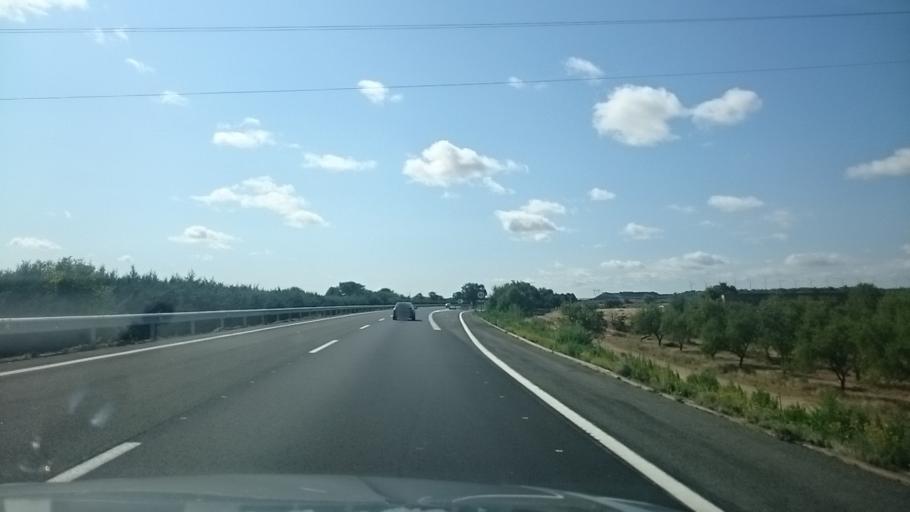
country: ES
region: Navarre
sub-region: Provincia de Navarra
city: Corella
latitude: 42.1193
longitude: -1.7409
